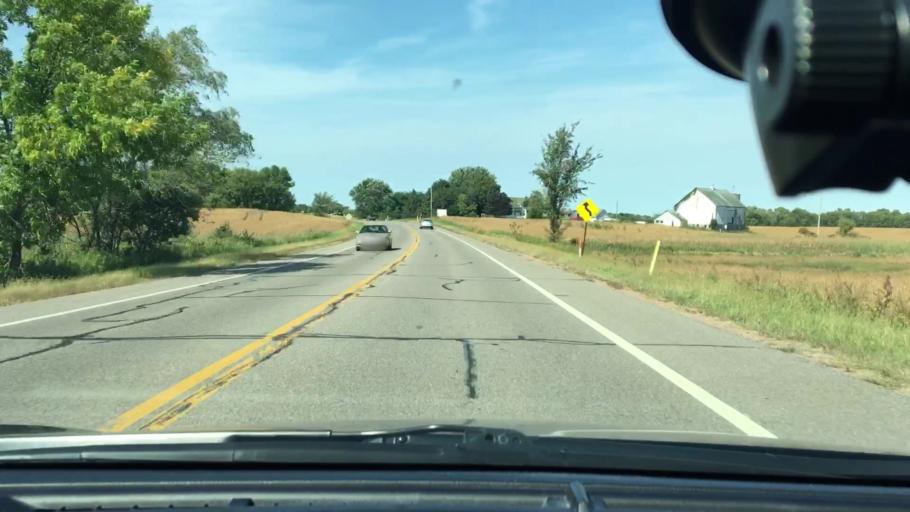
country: US
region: Minnesota
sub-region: Hennepin County
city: Corcoran
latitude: 45.0900
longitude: -93.5344
